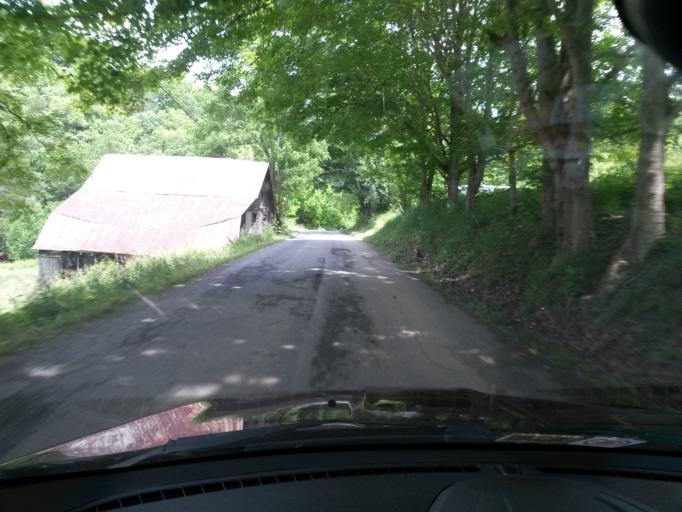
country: US
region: West Virginia
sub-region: Monroe County
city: Union
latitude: 37.5372
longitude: -80.5416
